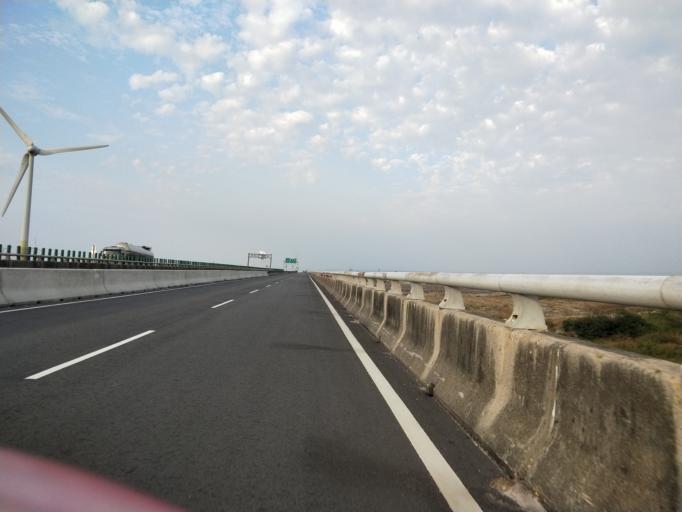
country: TW
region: Taiwan
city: Fengyuan
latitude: 24.4011
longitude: 120.6105
